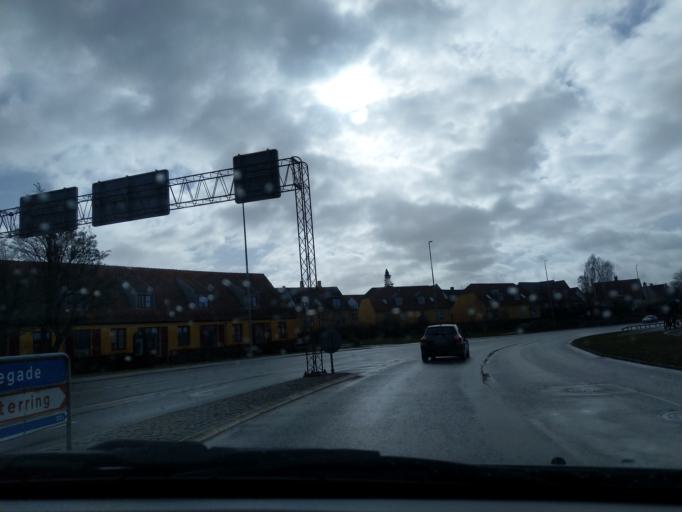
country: DK
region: Zealand
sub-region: Naestved Kommune
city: Naestved
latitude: 55.2274
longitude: 11.7576
